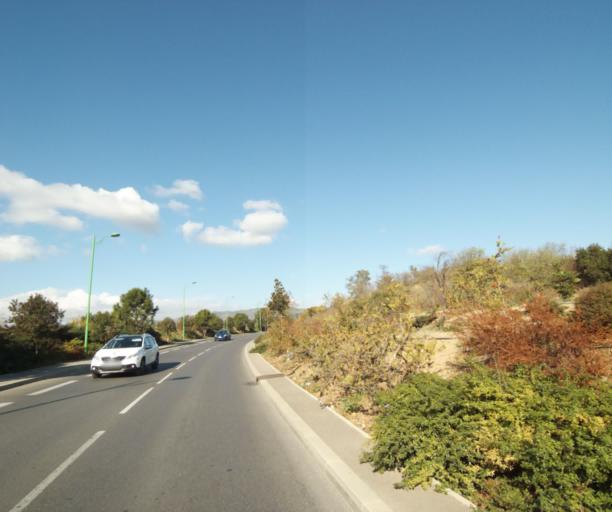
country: FR
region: Provence-Alpes-Cote d'Azur
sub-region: Departement des Bouches-du-Rhone
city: Allauch
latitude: 43.3365
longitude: 5.4750
